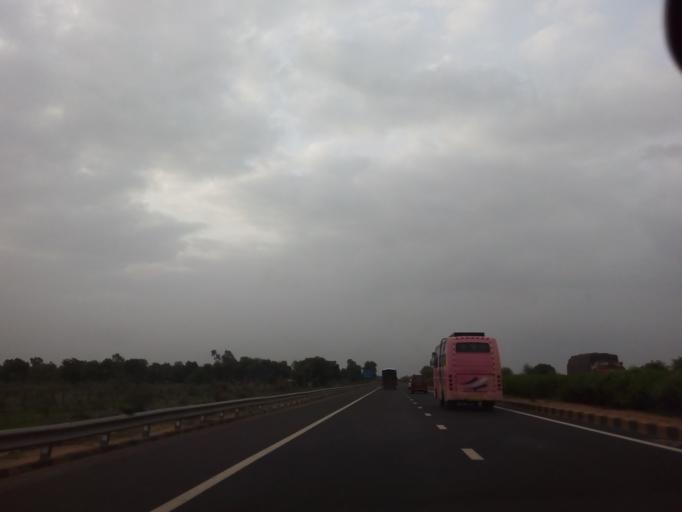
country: IN
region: Gujarat
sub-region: Kheda
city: Mahemdavad
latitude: 22.8923
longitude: 72.7841
